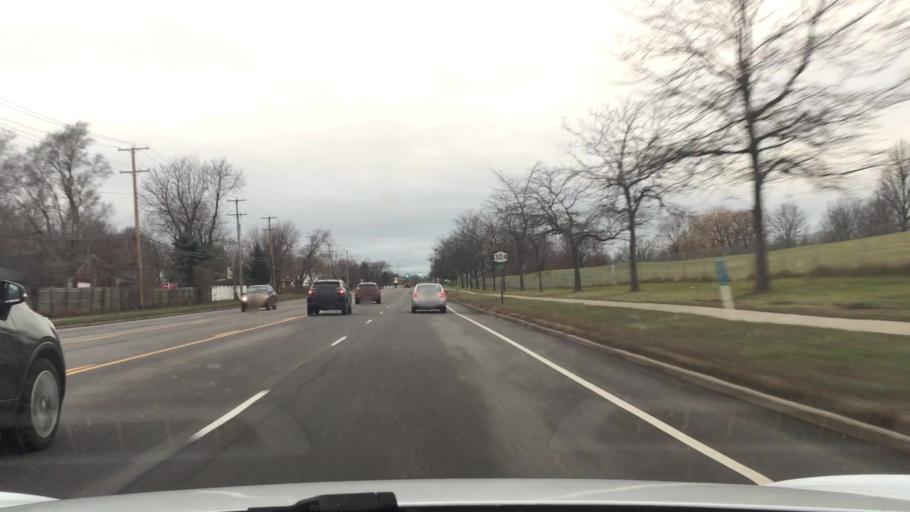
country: US
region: New York
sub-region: Erie County
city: Amherst
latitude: 42.9782
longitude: -78.7719
